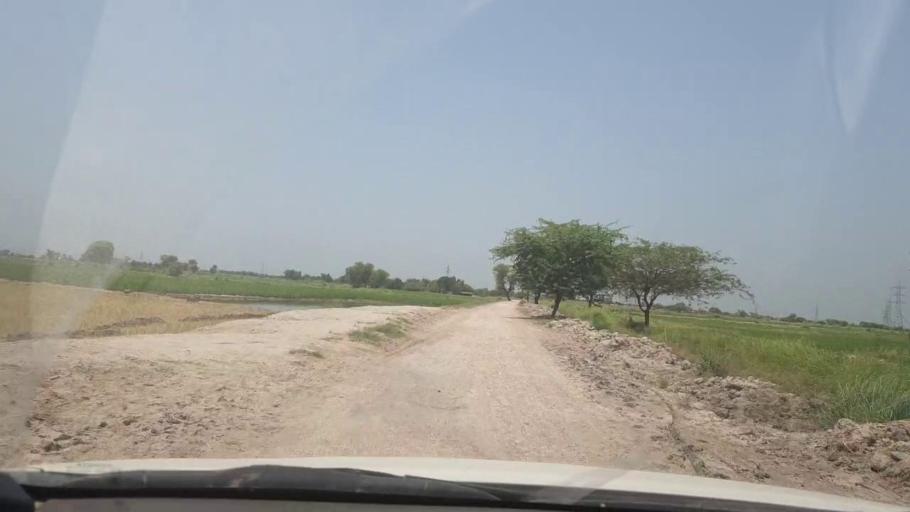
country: PK
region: Sindh
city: Lakhi
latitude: 27.8679
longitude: 68.6970
